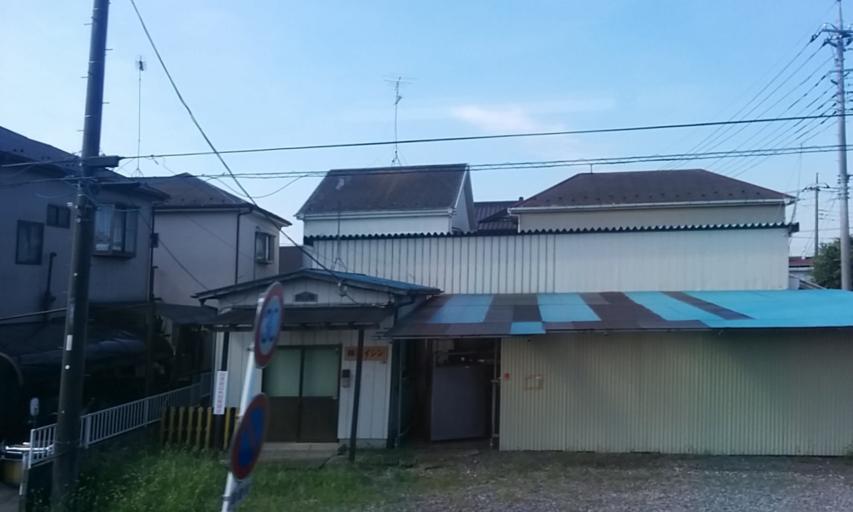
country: JP
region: Saitama
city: Kazo
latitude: 36.1133
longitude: 139.6235
